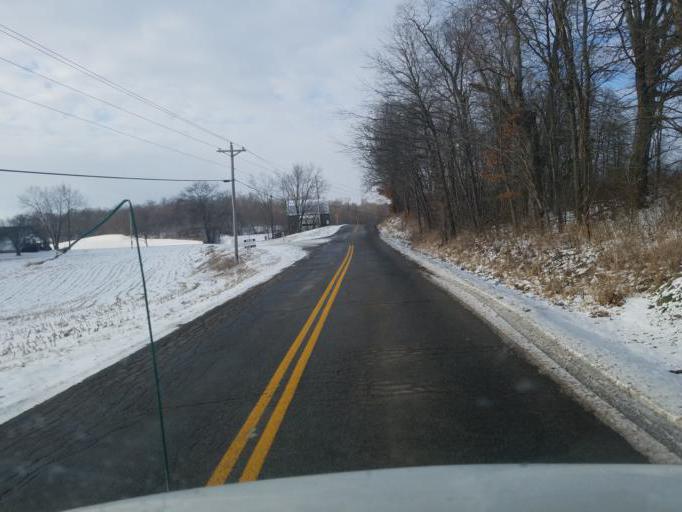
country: US
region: Ohio
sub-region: Holmes County
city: Millersburg
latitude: 40.4682
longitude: -81.9218
